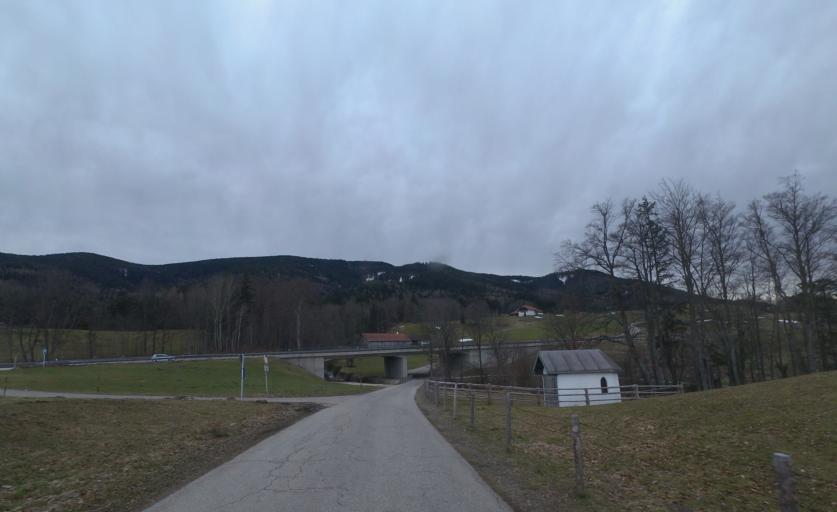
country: DE
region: Bavaria
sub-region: Upper Bavaria
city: Teisendorf
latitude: 47.8274
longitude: 12.7815
